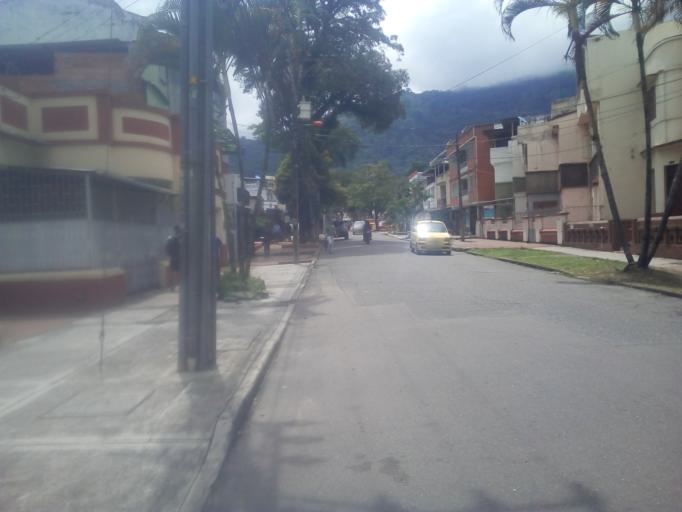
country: CO
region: Tolima
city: Ibague
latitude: 4.4486
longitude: -75.2427
